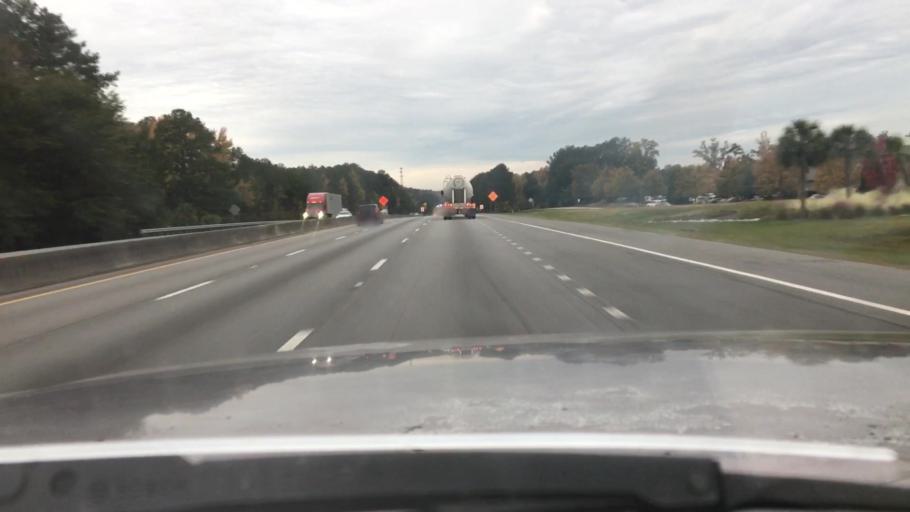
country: US
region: South Carolina
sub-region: Lexington County
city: Oak Grove
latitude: 34.0109
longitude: -81.1501
